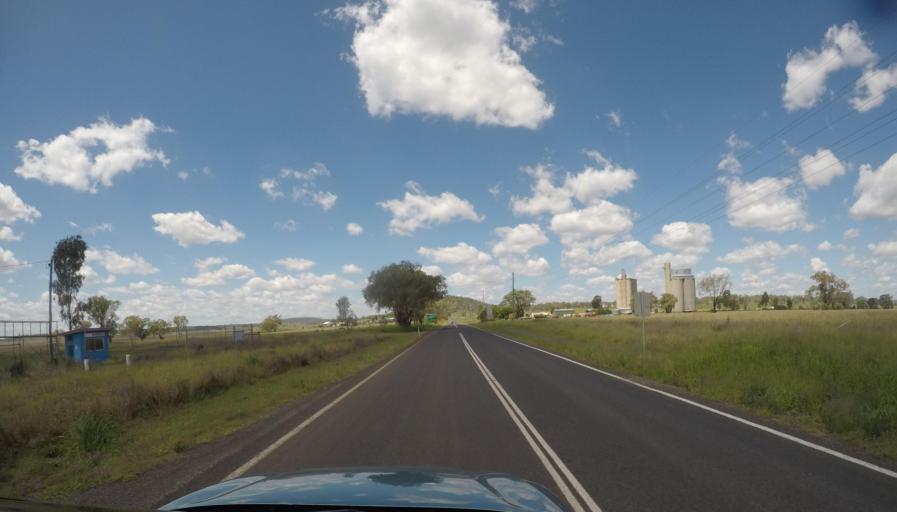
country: AU
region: Queensland
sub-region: Toowoomba
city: Oakey
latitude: -27.5350
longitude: 151.6280
